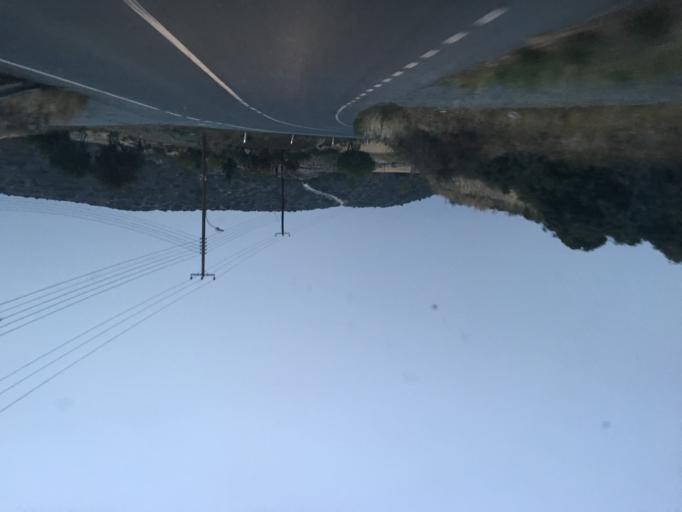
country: CY
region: Limassol
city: Parekklisha
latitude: 34.7313
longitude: 33.1601
